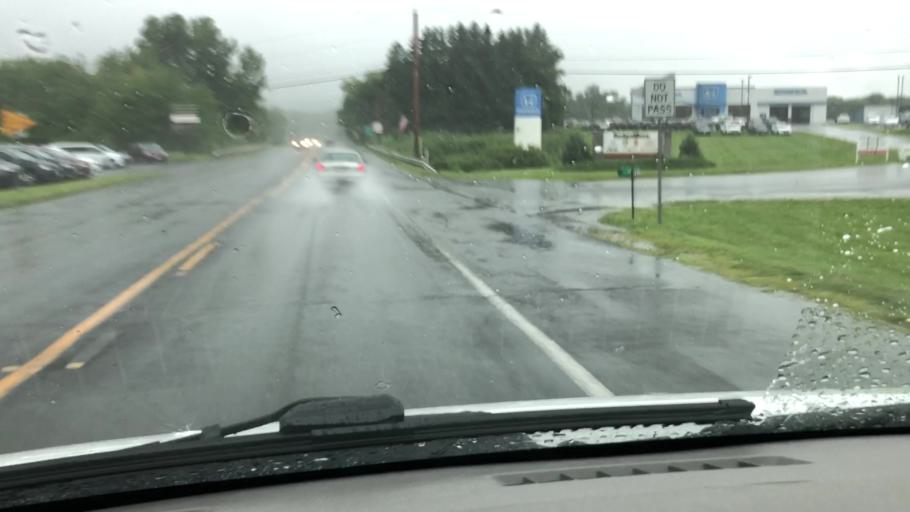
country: US
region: Massachusetts
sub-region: Berkshire County
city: Lanesborough
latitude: 42.5504
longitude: -73.1650
